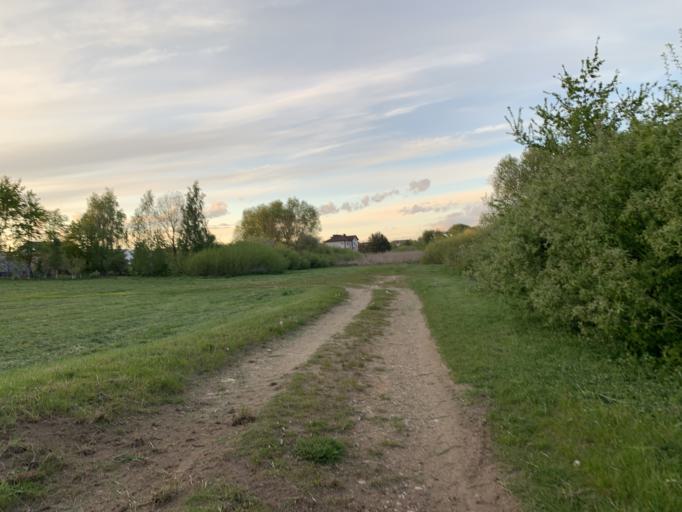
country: BY
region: Minsk
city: Nyasvizh
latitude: 53.2090
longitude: 26.6660
